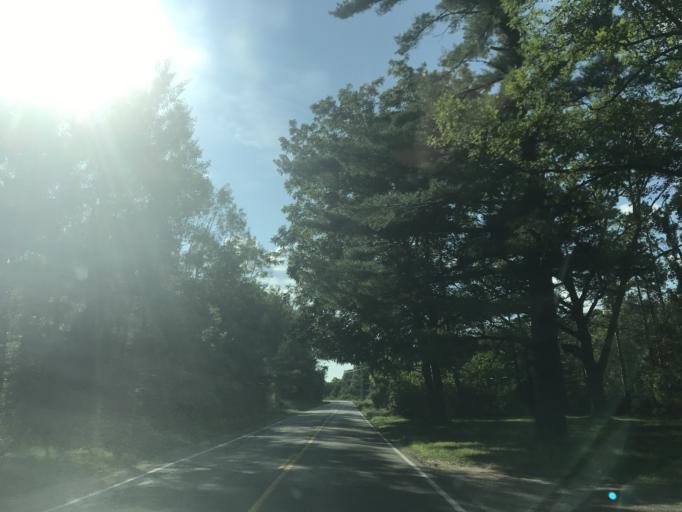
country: US
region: Michigan
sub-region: Newaygo County
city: Newaygo
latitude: 43.4265
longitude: -85.7742
